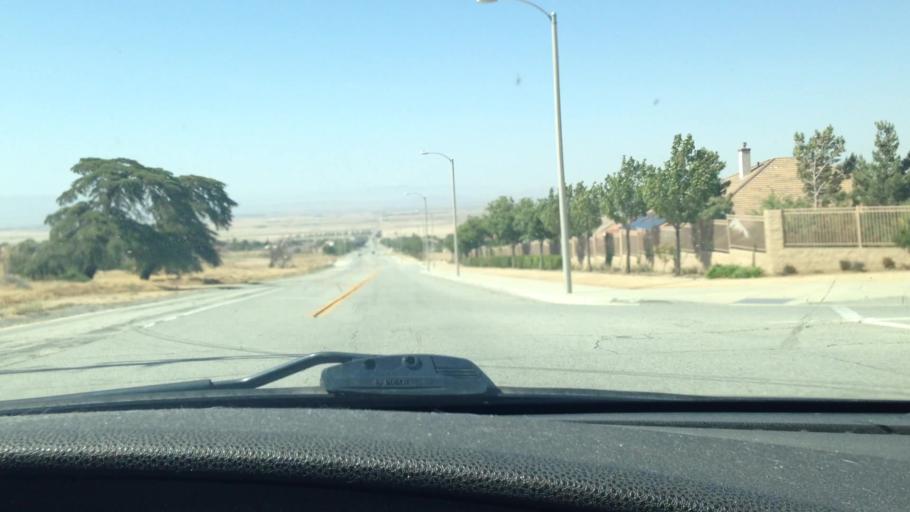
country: US
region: California
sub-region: Los Angeles County
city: Quartz Hill
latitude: 34.6382
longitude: -118.2535
